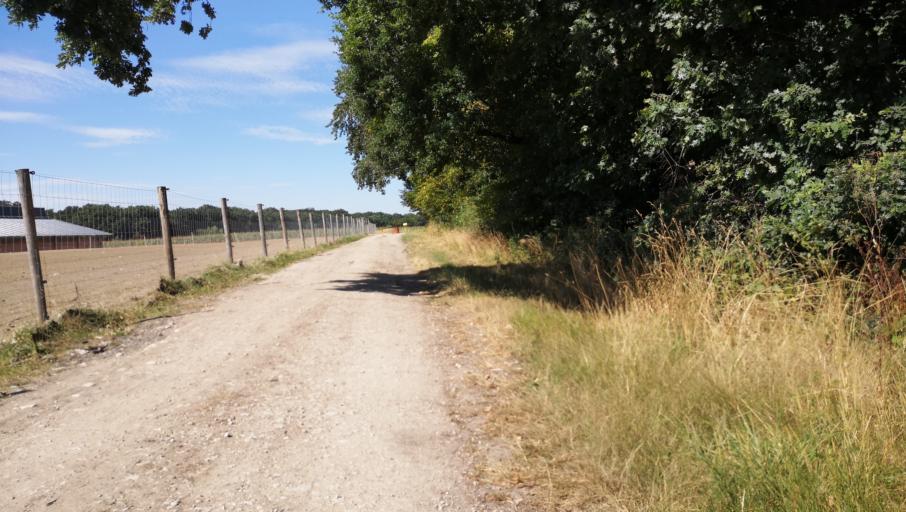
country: FR
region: Centre
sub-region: Departement du Loiret
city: Marigny-les-Usages
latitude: 47.9603
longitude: 2.0092
